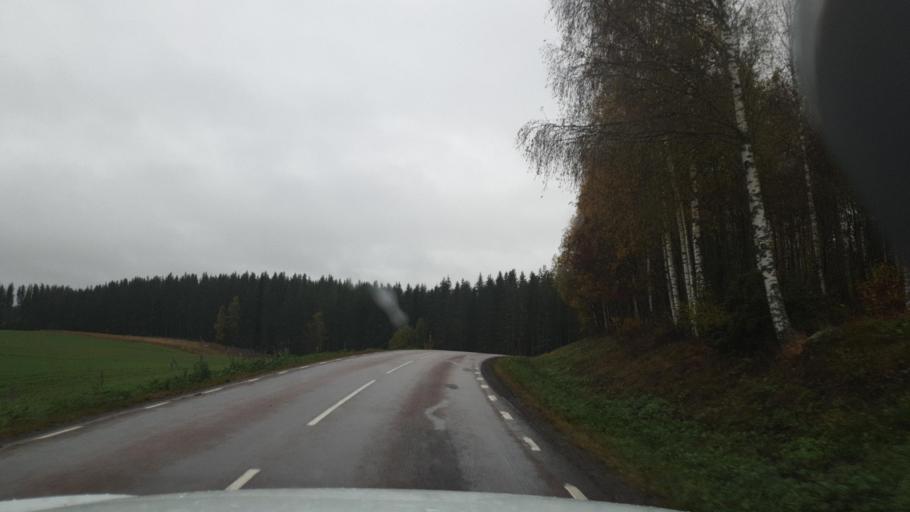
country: SE
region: Vaermland
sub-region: Eda Kommun
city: Charlottenberg
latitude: 59.8041
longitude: 12.2156
